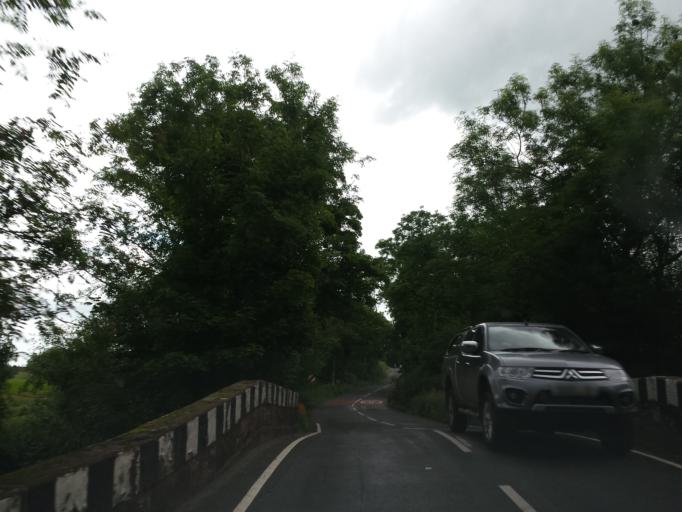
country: GB
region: Scotland
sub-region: Dumfries and Galloway
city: Dumfries
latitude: 55.0397
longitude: -3.6205
